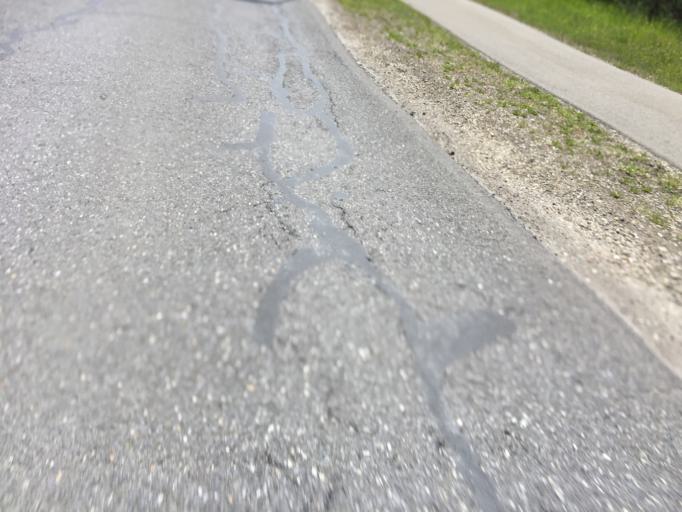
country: CH
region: Lucerne
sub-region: Entlebuch District
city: Escholzmatt
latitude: 46.8963
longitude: 7.9072
